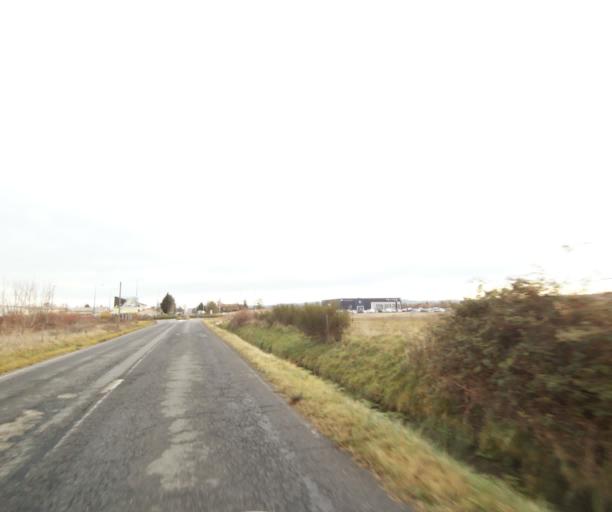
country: FR
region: Rhone-Alpes
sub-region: Departement de la Loire
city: Bonson
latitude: 45.5161
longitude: 4.2007
